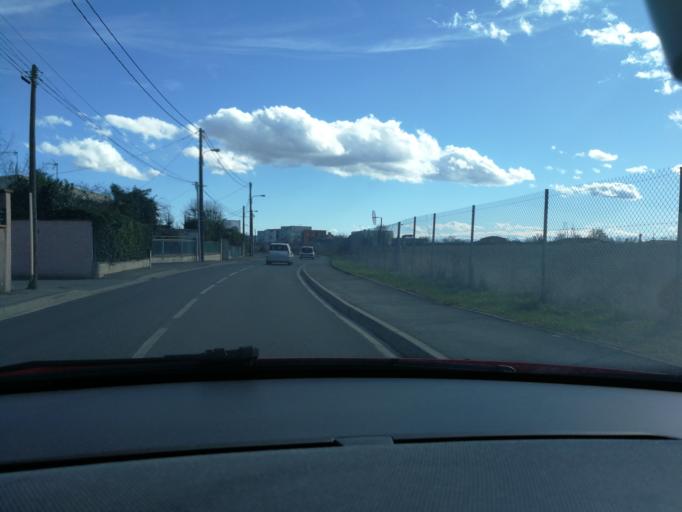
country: FR
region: Midi-Pyrenees
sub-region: Departement de la Haute-Garonne
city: Portet-sur-Garonne
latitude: 43.5474
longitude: 1.3853
